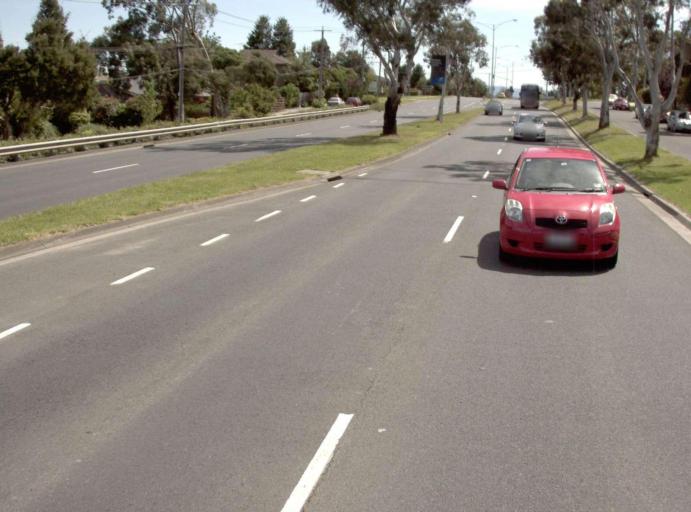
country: AU
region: Victoria
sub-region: Manningham
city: Donvale
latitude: -37.7800
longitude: 145.1637
